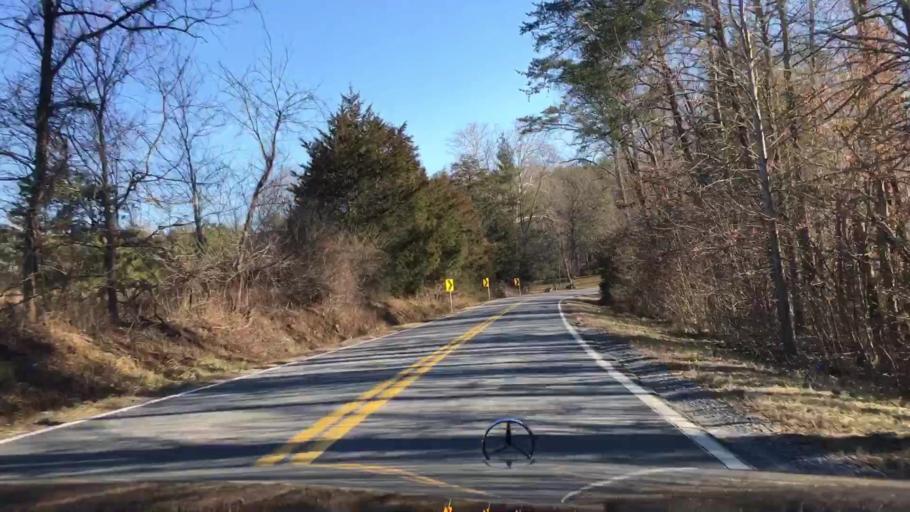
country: US
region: Virginia
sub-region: Campbell County
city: Altavista
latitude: 37.1452
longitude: -79.3226
